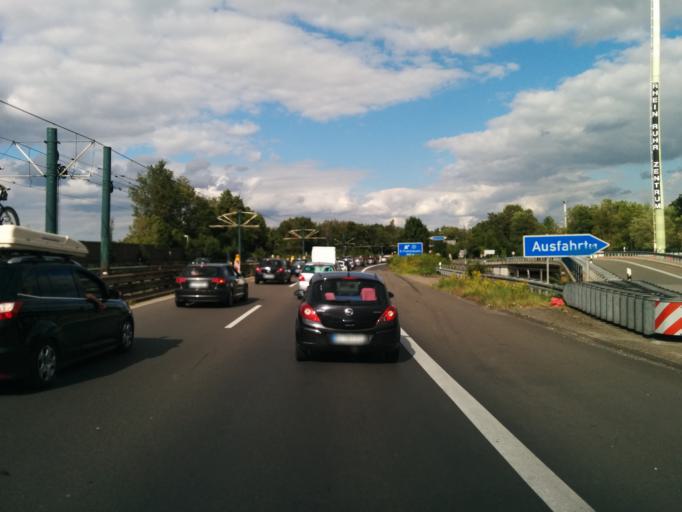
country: DE
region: North Rhine-Westphalia
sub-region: Regierungsbezirk Dusseldorf
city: Essen
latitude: 51.4398
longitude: 6.9526
